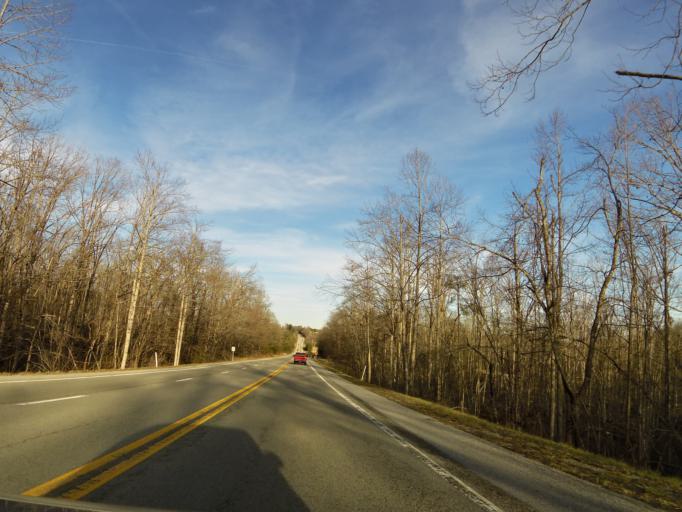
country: US
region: Tennessee
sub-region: Cumberland County
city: Crossville
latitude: 35.9708
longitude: -85.2047
